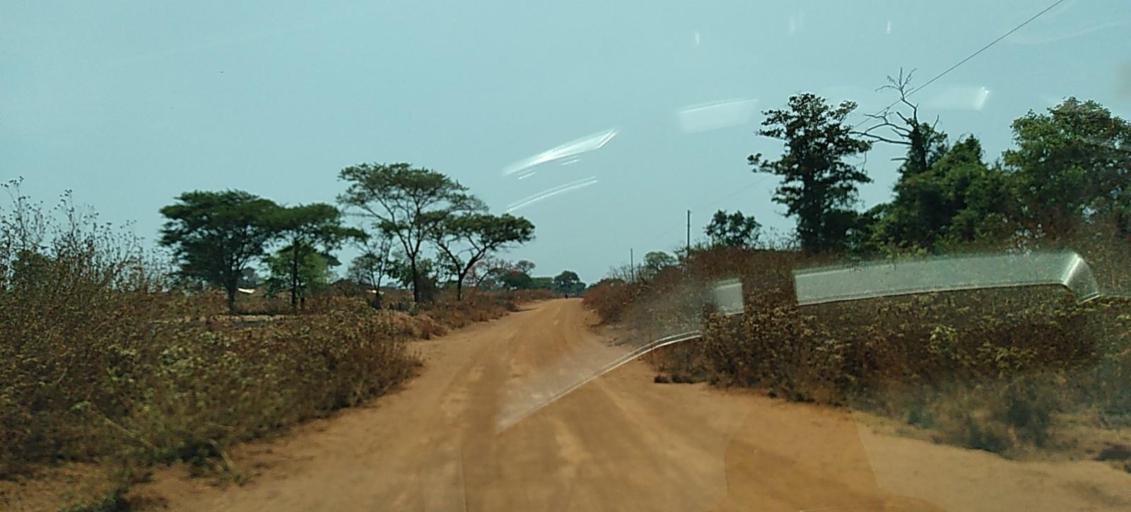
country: CD
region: Katanga
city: Kipushi
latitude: -11.9367
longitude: 26.9579
